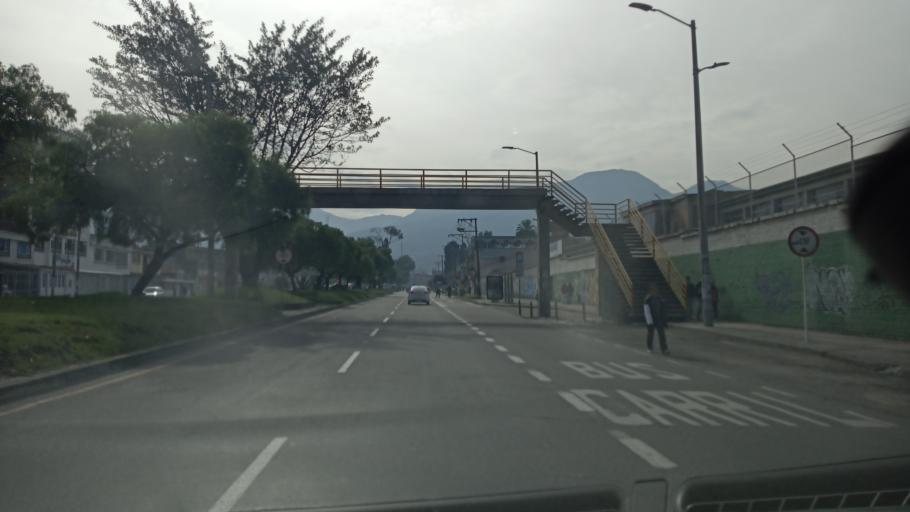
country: CO
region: Bogota D.C.
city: Bogota
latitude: 4.5783
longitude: -74.0983
